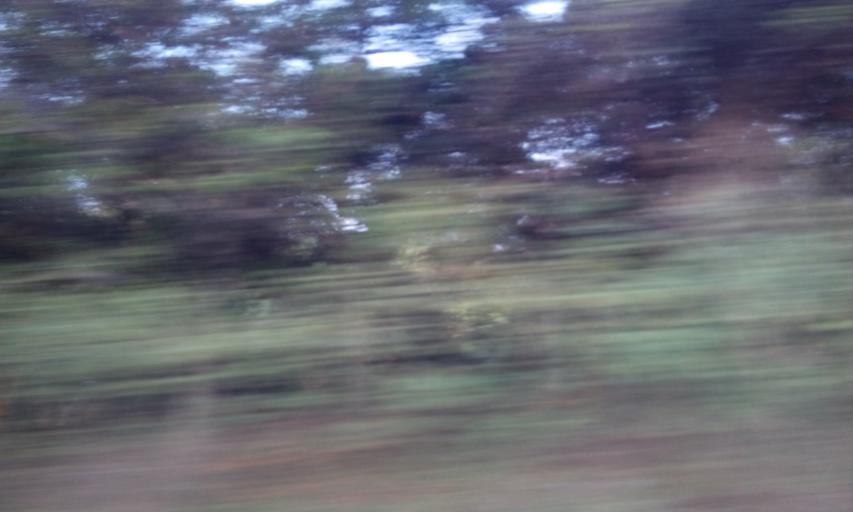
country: TH
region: Trat
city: Laem Ngop
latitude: 12.1953
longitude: 102.2888
